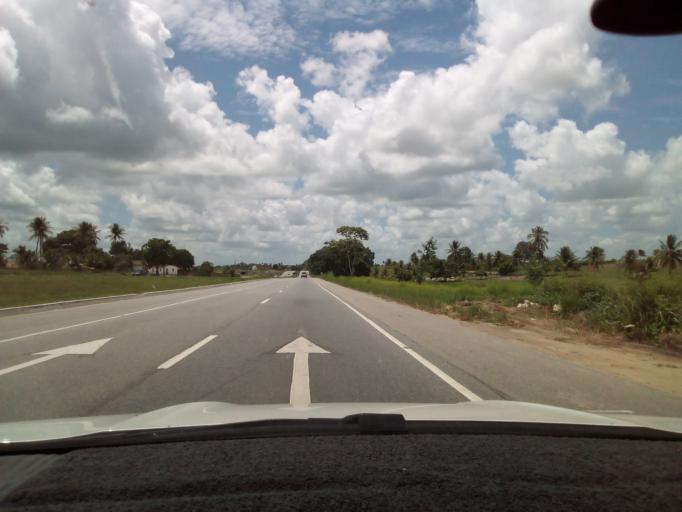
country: BR
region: Paraiba
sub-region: Pilar
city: Pilar
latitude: -7.1881
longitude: -35.2824
